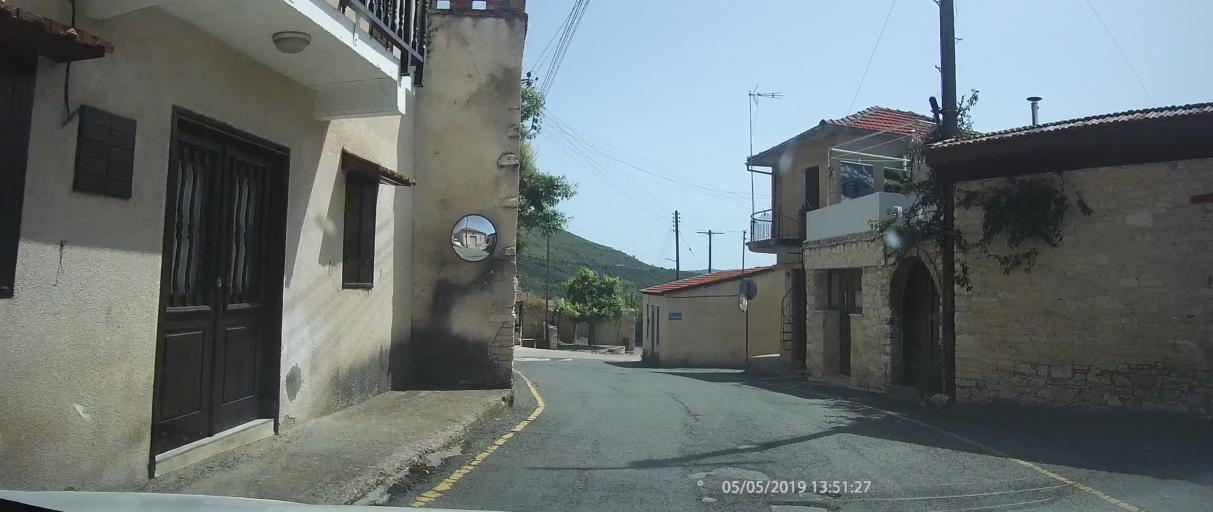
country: CY
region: Limassol
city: Pachna
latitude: 34.8366
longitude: 32.7365
